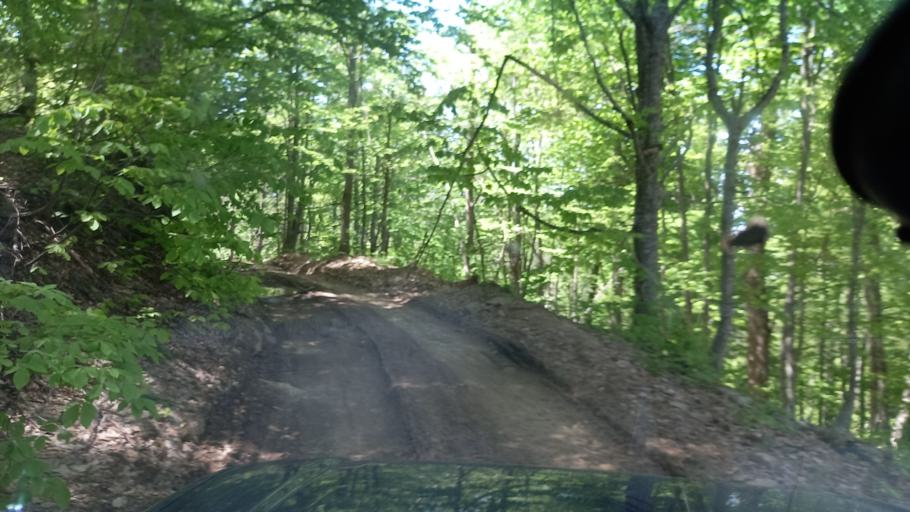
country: RU
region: Krasnodarskiy
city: Tuapse
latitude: 44.2501
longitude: 39.2969
